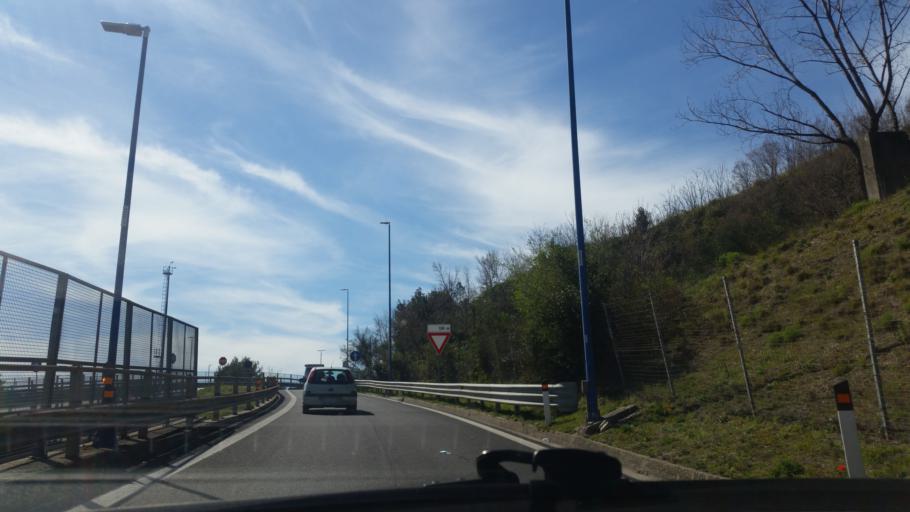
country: IT
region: Campania
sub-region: Provincia di Napoli
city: Napoli
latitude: 40.8656
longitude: 14.2414
